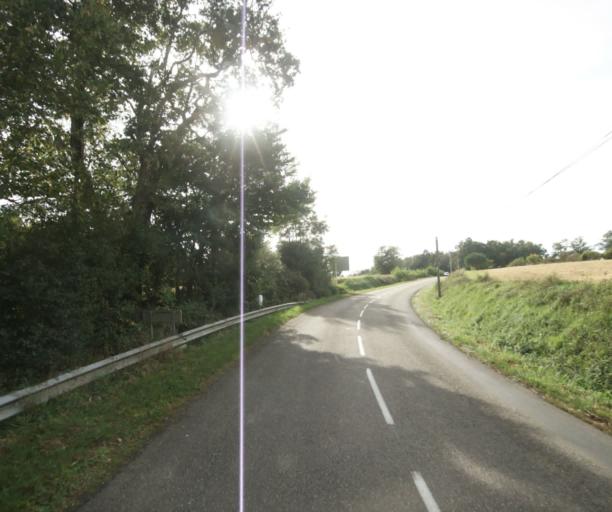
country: FR
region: Midi-Pyrenees
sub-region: Departement du Gers
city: Cazaubon
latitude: 43.8598
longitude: -0.1234
